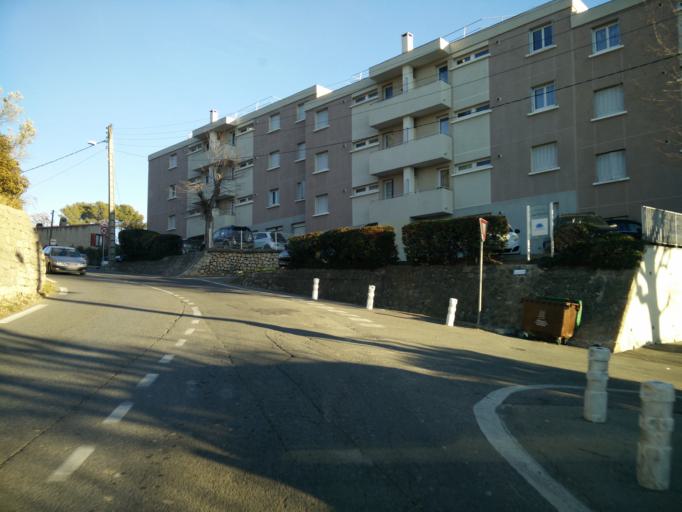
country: FR
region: Provence-Alpes-Cote d'Azur
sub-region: Departement du Var
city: Draguignan
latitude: 43.5401
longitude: 6.4725
